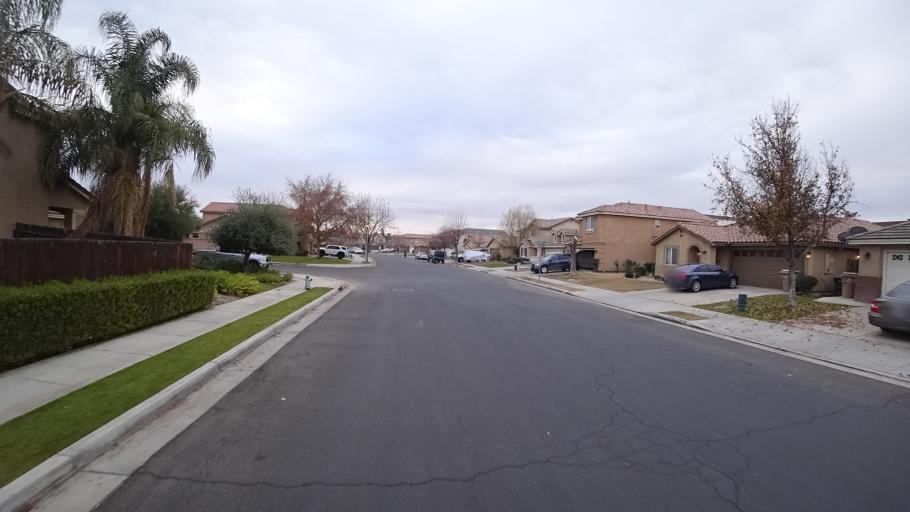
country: US
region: California
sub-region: Kern County
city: Greenfield
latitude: 35.2984
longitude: -119.0742
